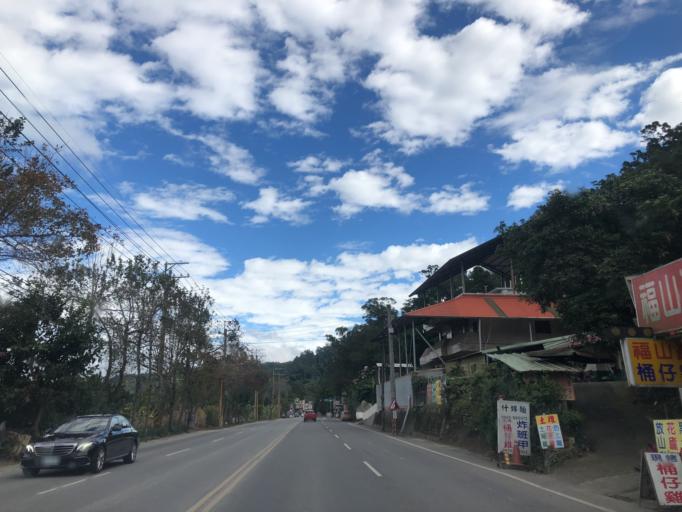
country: TW
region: Taiwan
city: Daxi
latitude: 24.8245
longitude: 121.2625
